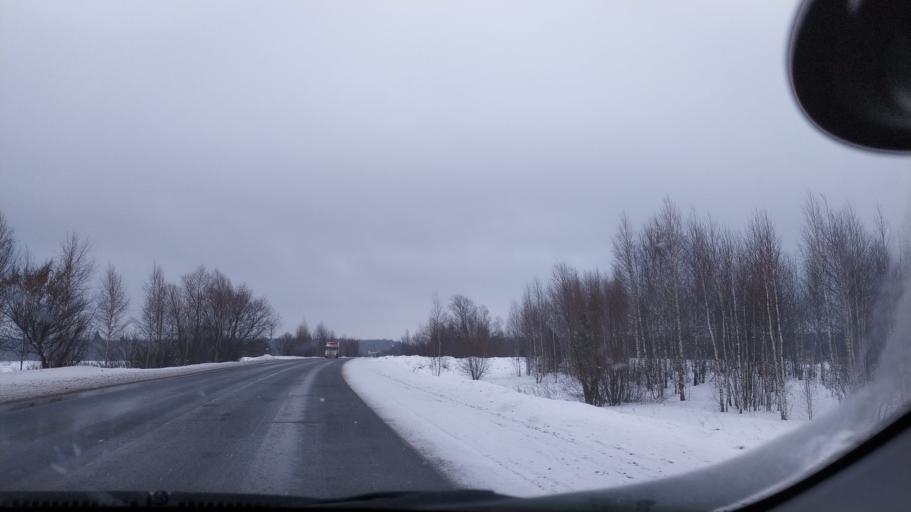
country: RU
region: Mariy-El
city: Krasnogorskiy
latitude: 56.1641
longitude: 48.1804
